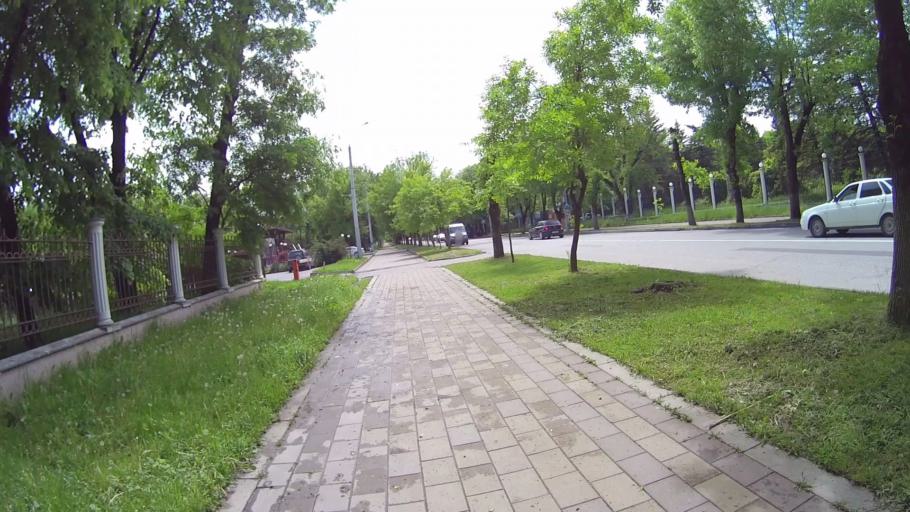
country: RU
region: Kabardino-Balkariya
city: Vol'nyy Aul
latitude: 43.4612
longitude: 43.5867
